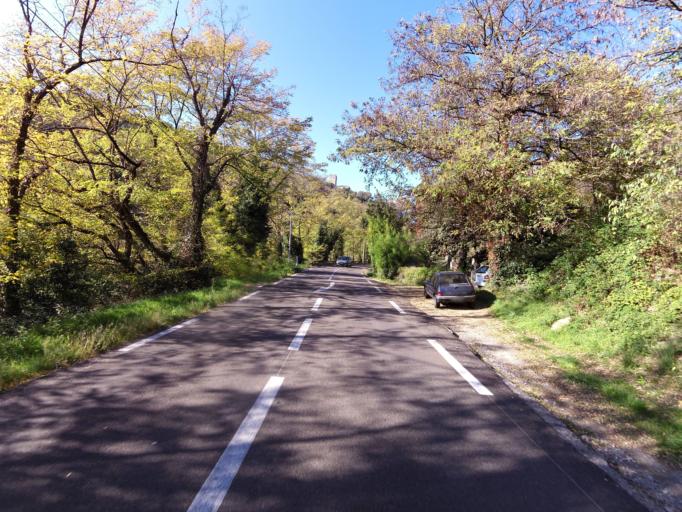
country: FR
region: Rhone-Alpes
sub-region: Departement de l'Ardeche
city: Largentiere
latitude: 44.5266
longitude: 4.2989
